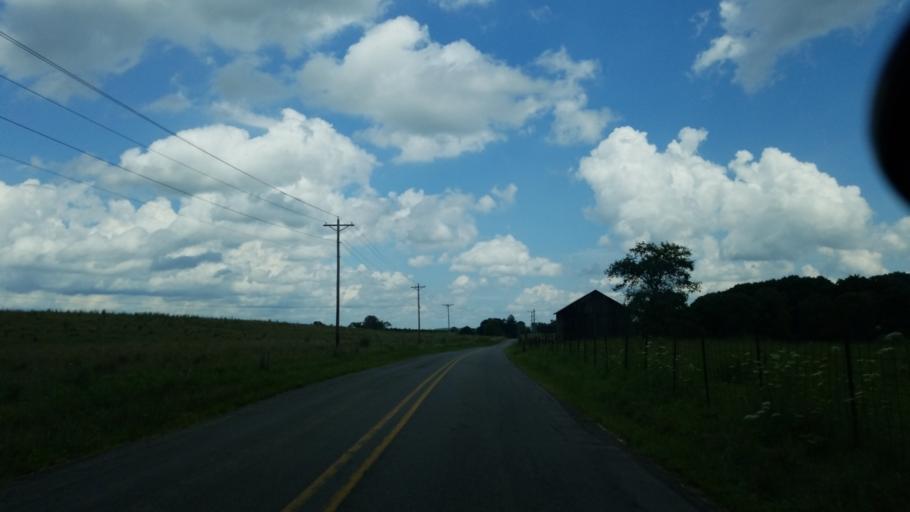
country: US
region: Pennsylvania
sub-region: Jefferson County
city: Brookville
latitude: 41.2389
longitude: -79.0389
